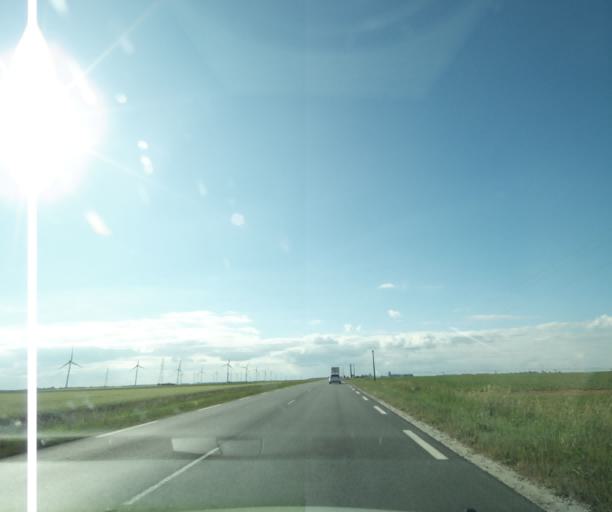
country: FR
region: Centre
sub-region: Departement d'Eure-et-Loir
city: Voves
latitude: 48.3060
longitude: 1.6917
